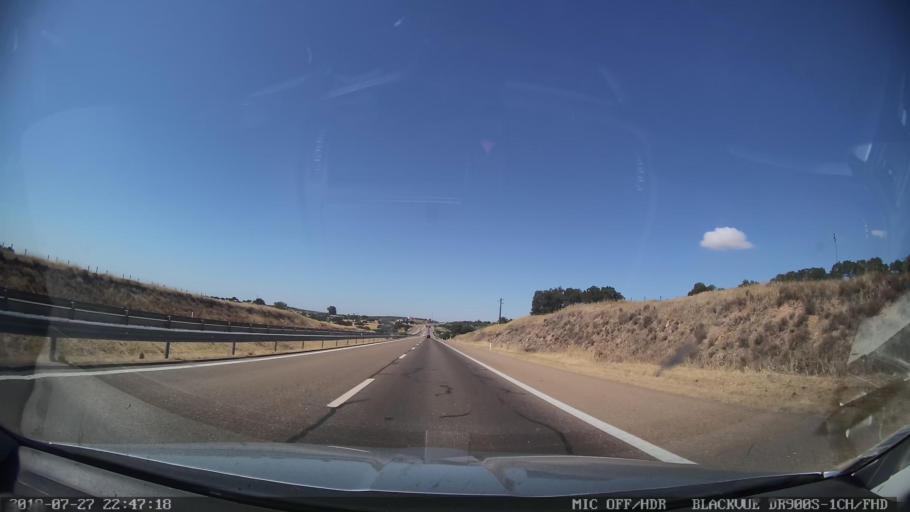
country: PT
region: Portalegre
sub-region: Elvas
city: Elvas
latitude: 38.8971
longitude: -7.2068
